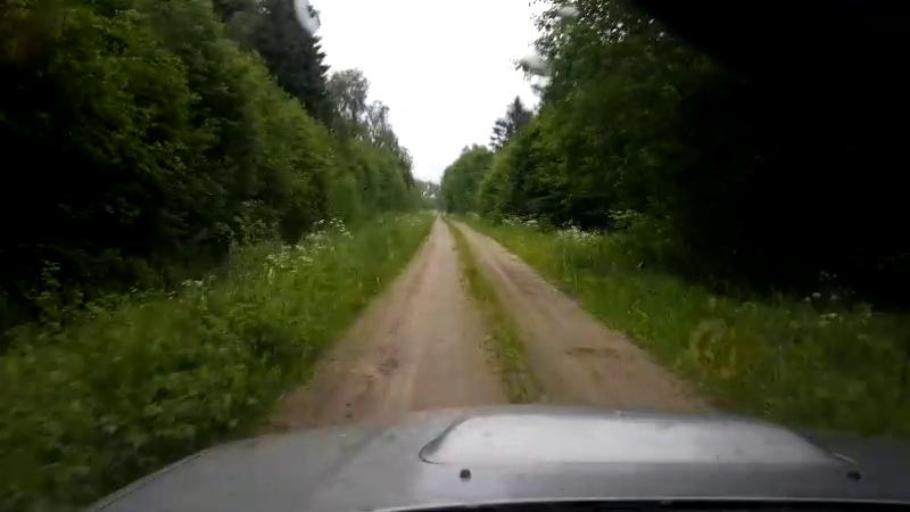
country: EE
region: Paernumaa
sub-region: Tootsi vald
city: Tootsi
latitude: 58.5839
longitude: 24.6499
